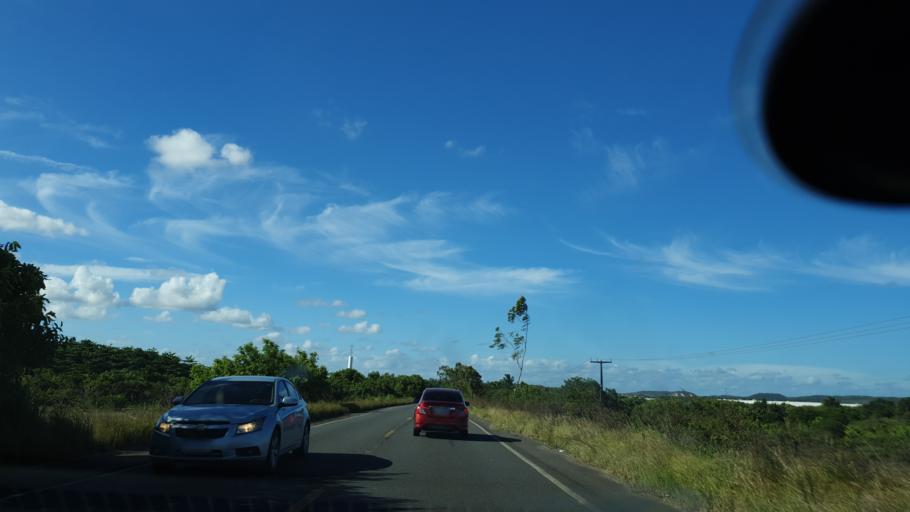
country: BR
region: Bahia
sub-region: Camacari
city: Camacari
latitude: -12.6505
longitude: -38.3035
